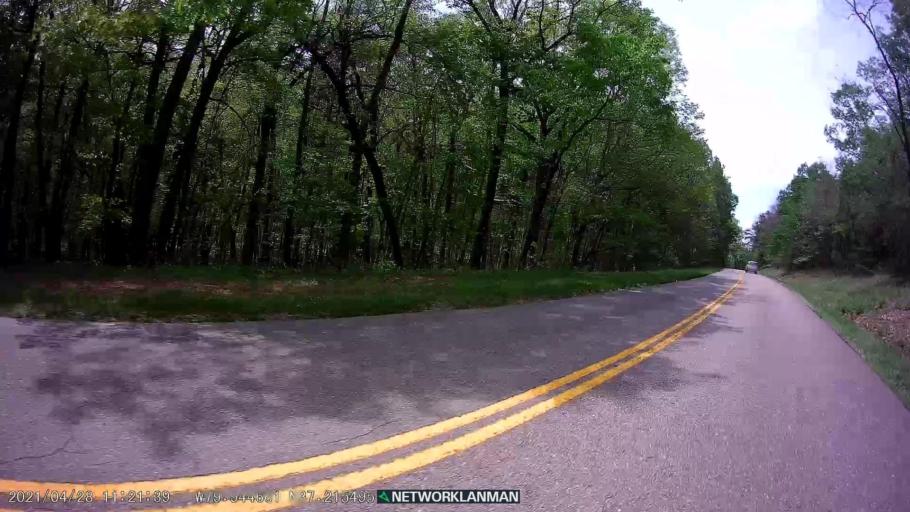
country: US
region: Virginia
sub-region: Roanoke County
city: Narrows
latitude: 37.2158
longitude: -79.9446
